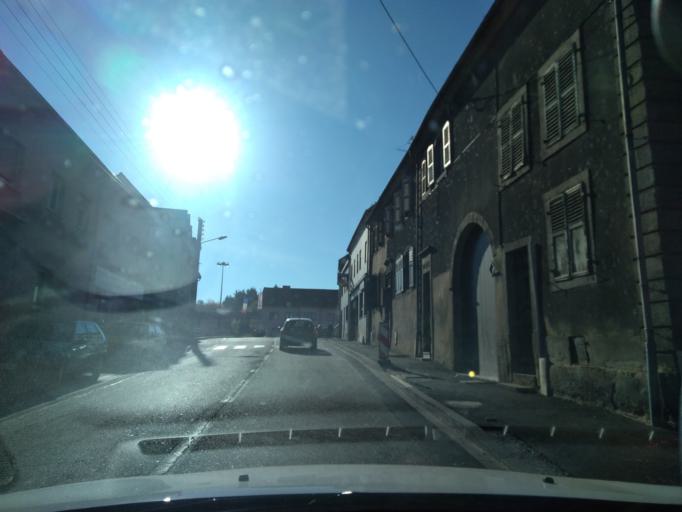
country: FR
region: Lorraine
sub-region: Departement de la Moselle
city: Sarreguemines
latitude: 49.1137
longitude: 7.0463
